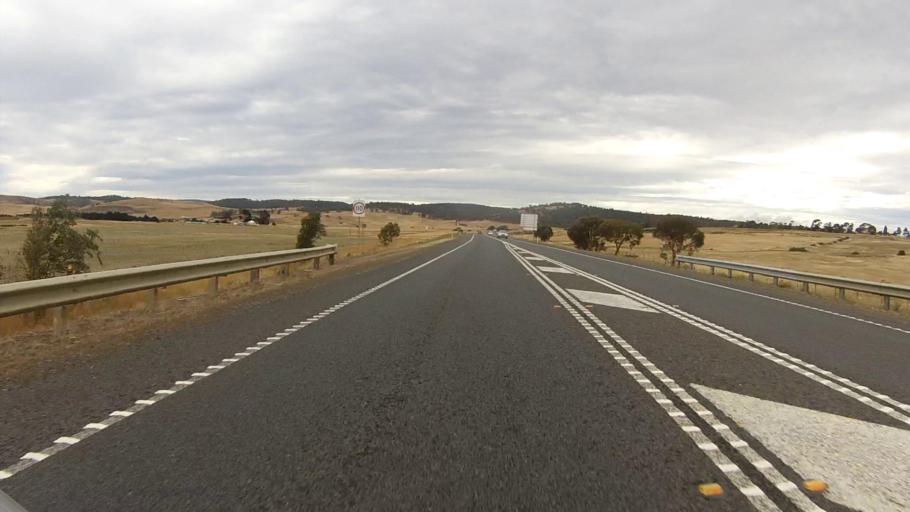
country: AU
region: Tasmania
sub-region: Brighton
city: Bridgewater
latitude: -42.3070
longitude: 147.3576
